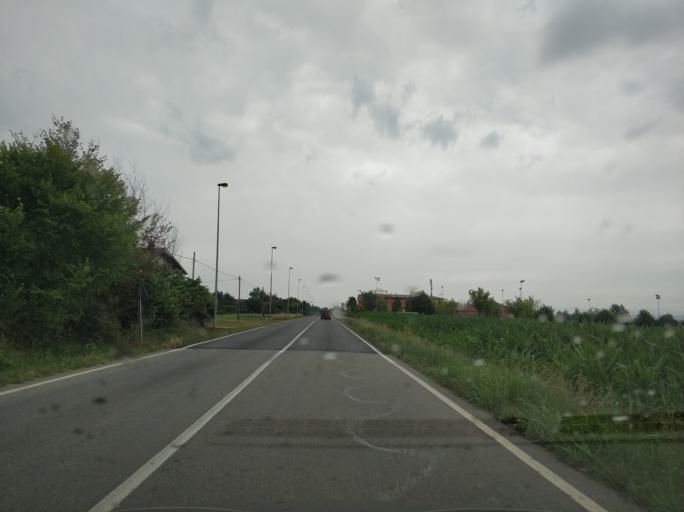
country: IT
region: Piedmont
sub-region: Provincia di Torino
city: Pralormo
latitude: 44.8715
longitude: 7.8936
